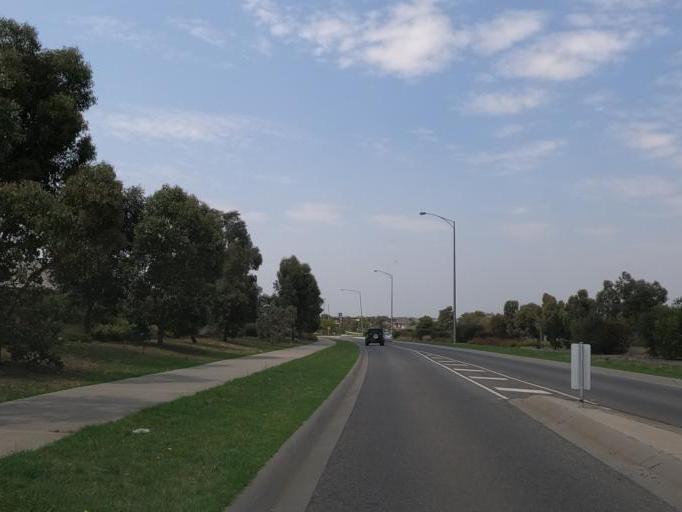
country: AU
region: Victoria
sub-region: Hume
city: Craigieburn
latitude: -37.5695
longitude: 144.9201
